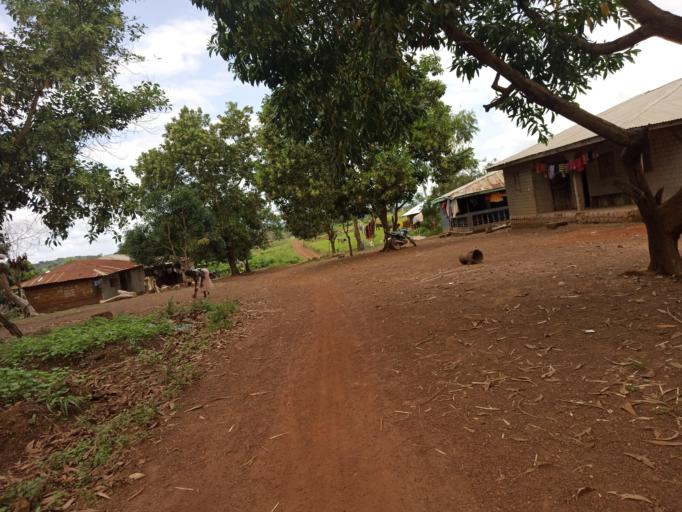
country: SL
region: Northern Province
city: Kamakwie
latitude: 9.4816
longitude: -12.2430
